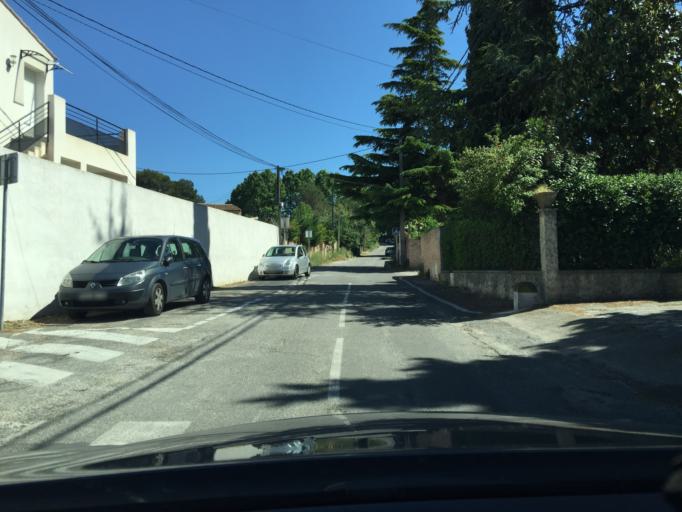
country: FR
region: Provence-Alpes-Cote d'Azur
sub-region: Departement des Bouches-du-Rhone
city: La Penne-sur-Huveaune
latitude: 43.2804
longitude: 5.5430
